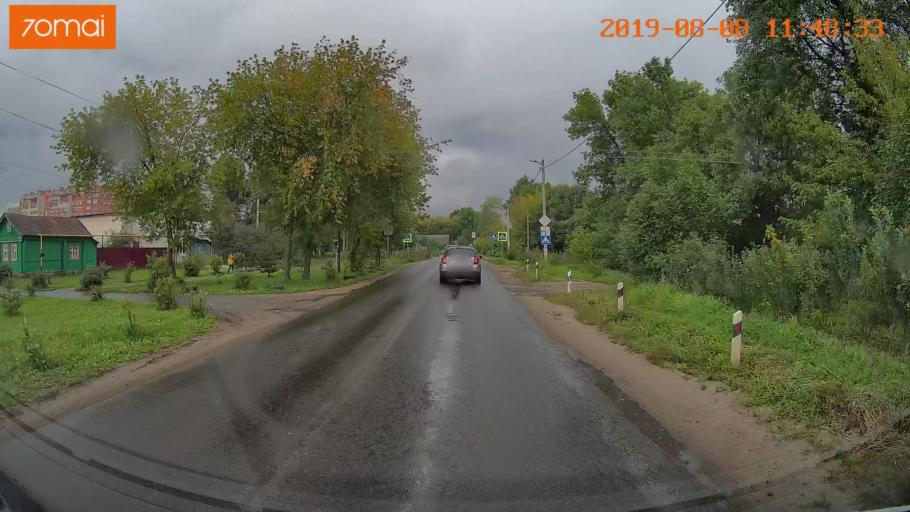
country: RU
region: Ivanovo
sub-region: Gorod Ivanovo
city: Ivanovo
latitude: 56.9748
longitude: 40.9839
